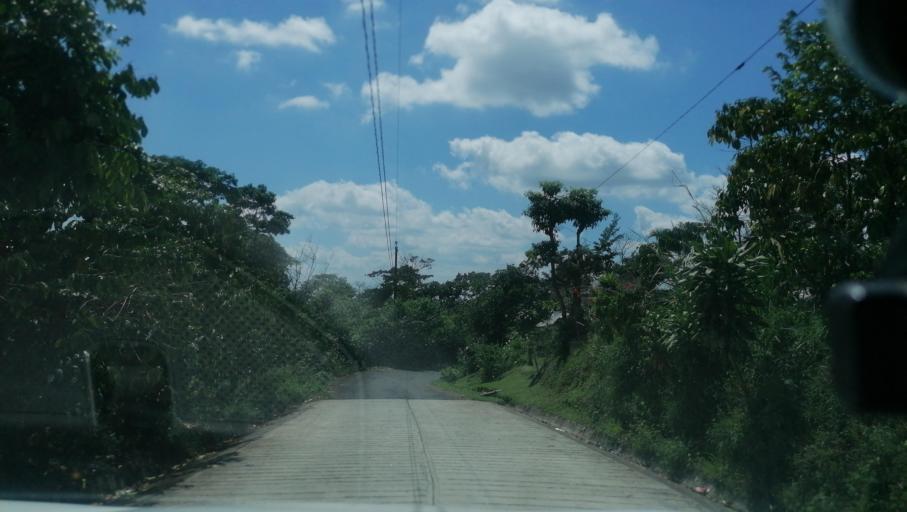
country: MX
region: Chiapas
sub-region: Cacahoatan
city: Benito Juarez
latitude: 15.0610
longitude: -92.1453
